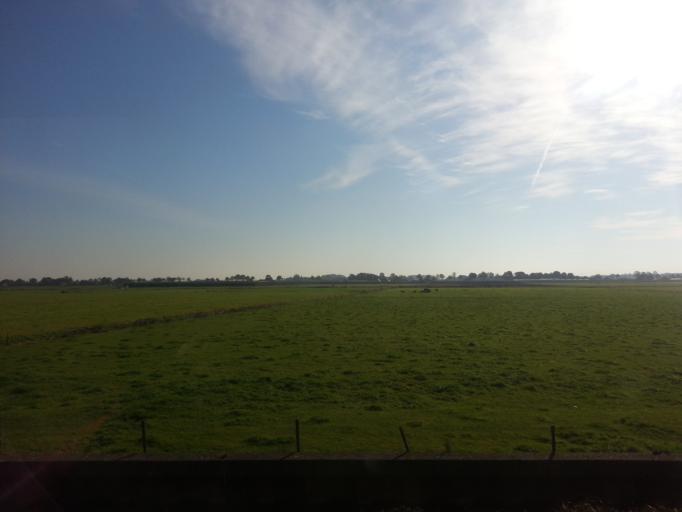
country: NL
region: Gelderland
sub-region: Gemeente Neerijnen
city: Neerijnen
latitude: 51.8540
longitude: 5.2593
